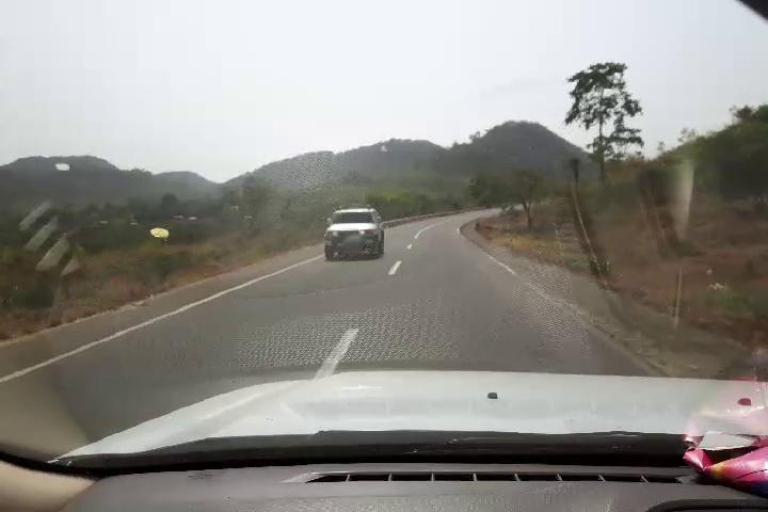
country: SL
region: Western Area
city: Waterloo
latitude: 8.2061
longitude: -13.1306
